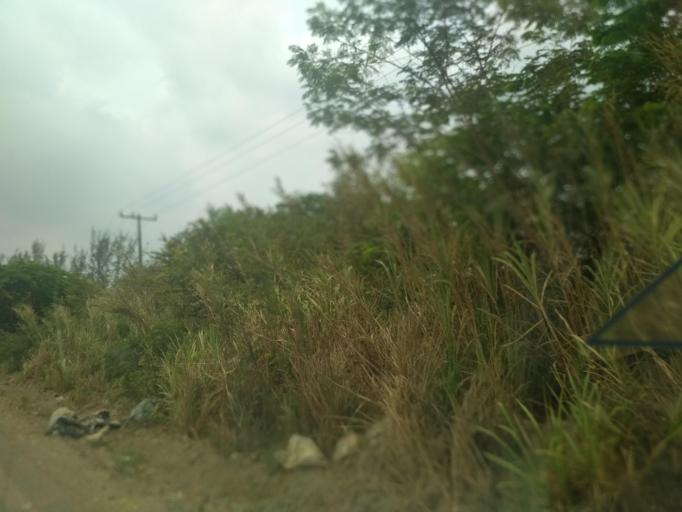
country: MX
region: Veracruz
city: Paso del Toro
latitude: 19.0133
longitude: -96.1339
